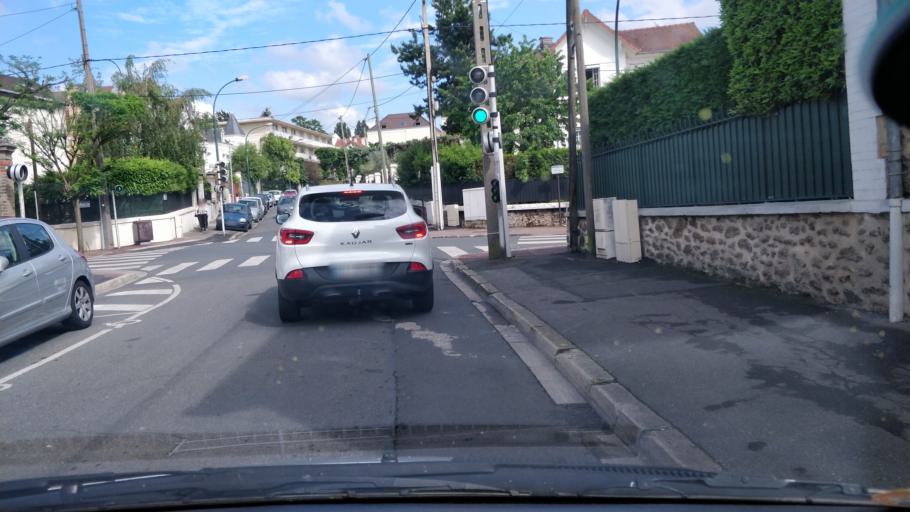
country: FR
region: Ile-de-France
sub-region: Departement de Seine-Saint-Denis
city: Le Raincy
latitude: 48.8978
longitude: 2.5125
